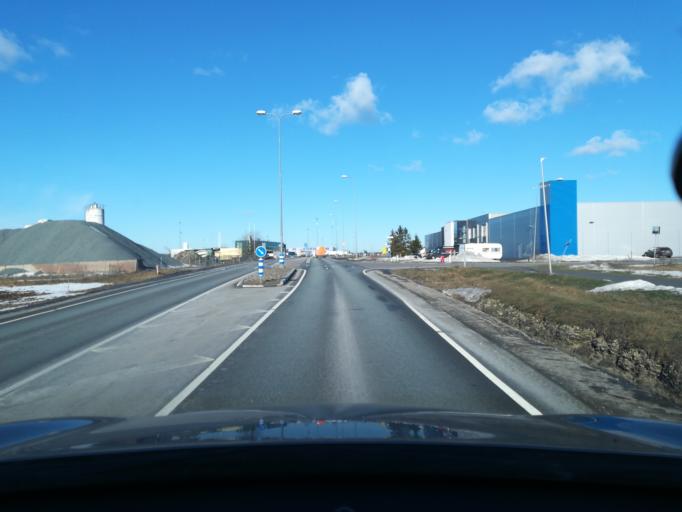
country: EE
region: Harju
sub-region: Saue vald
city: Laagri
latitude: 59.3352
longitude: 24.6210
